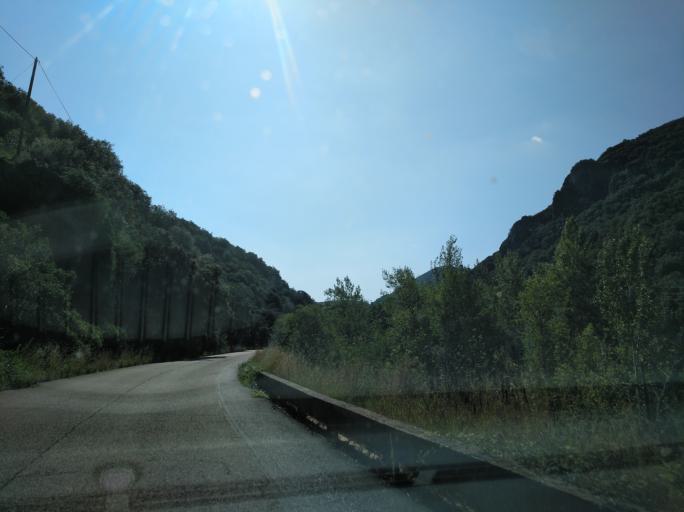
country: ES
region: Catalonia
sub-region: Provincia de Girona
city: la Cellera de Ter
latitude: 41.9857
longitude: 2.5788
